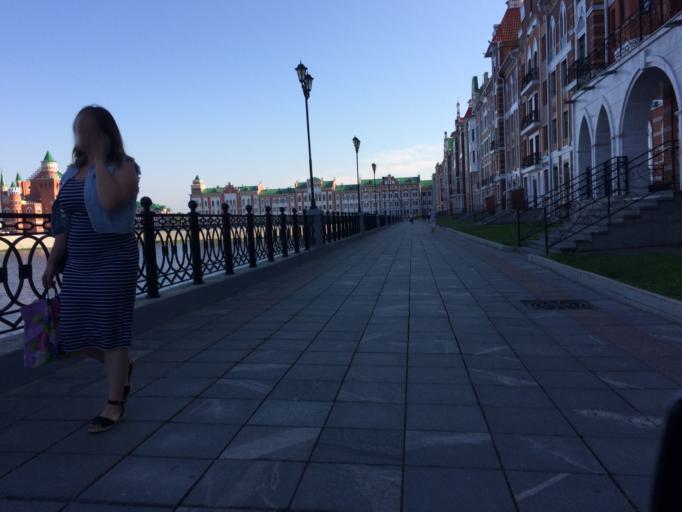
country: RU
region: Mariy-El
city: Yoshkar-Ola
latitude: 56.6341
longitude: 47.9099
